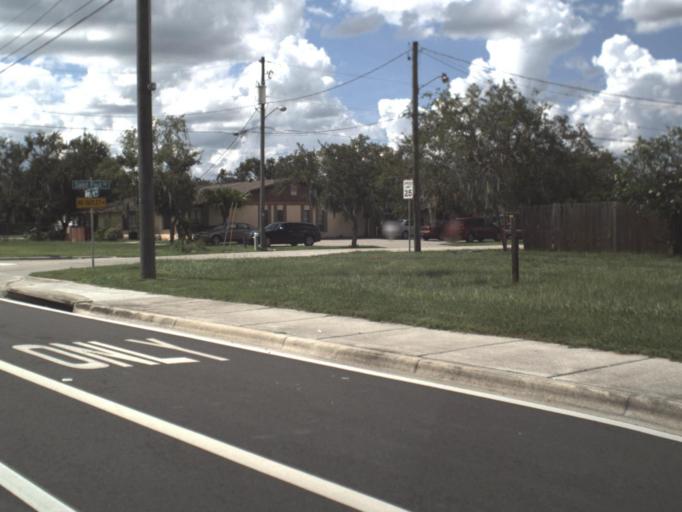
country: US
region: Florida
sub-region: Polk County
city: Jan-Phyl Village
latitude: 28.0050
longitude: -81.7822
